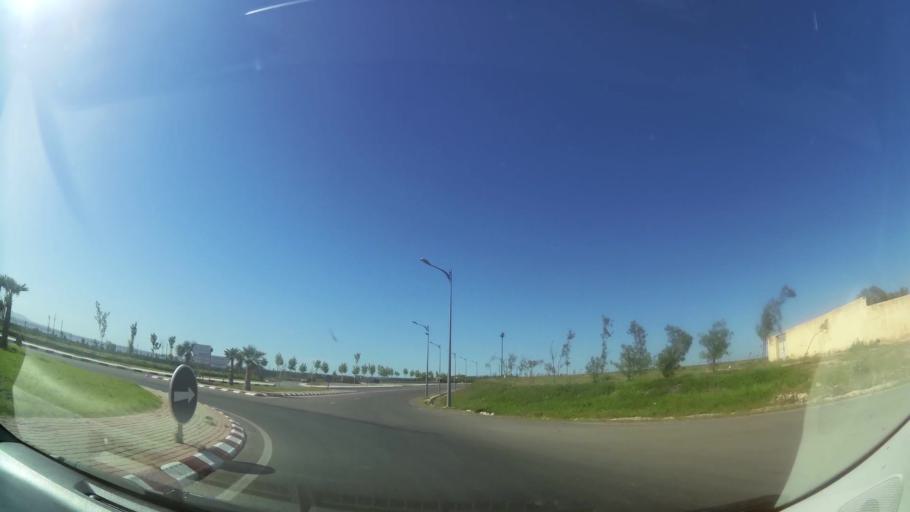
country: MA
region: Oriental
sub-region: Oujda-Angad
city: Oujda
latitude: 34.7373
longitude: -1.9188
